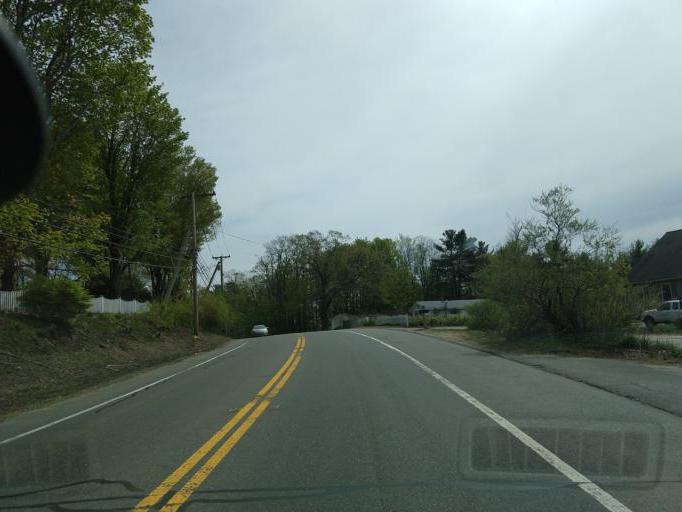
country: US
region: Massachusetts
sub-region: Essex County
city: Merrimac
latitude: 42.8403
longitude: -70.9674
